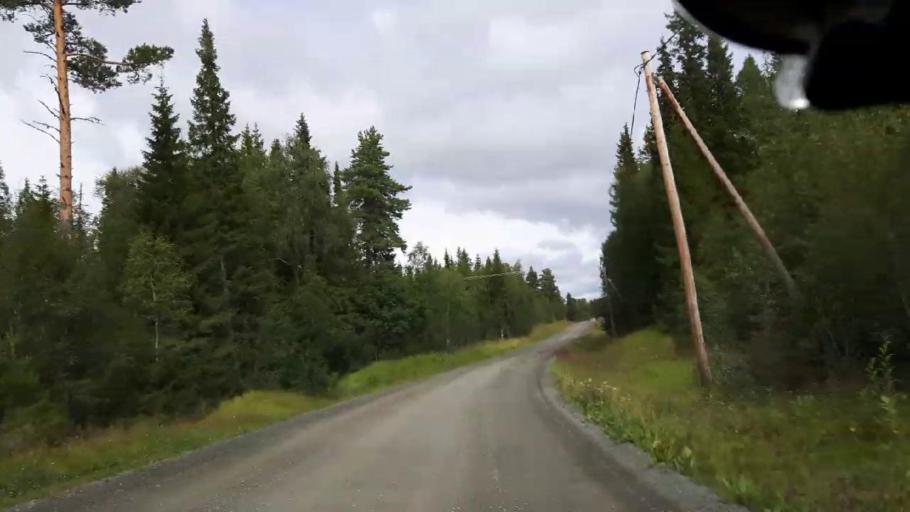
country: SE
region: Jaemtland
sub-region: Krokoms Kommun
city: Valla
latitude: 63.4023
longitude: 14.0941
